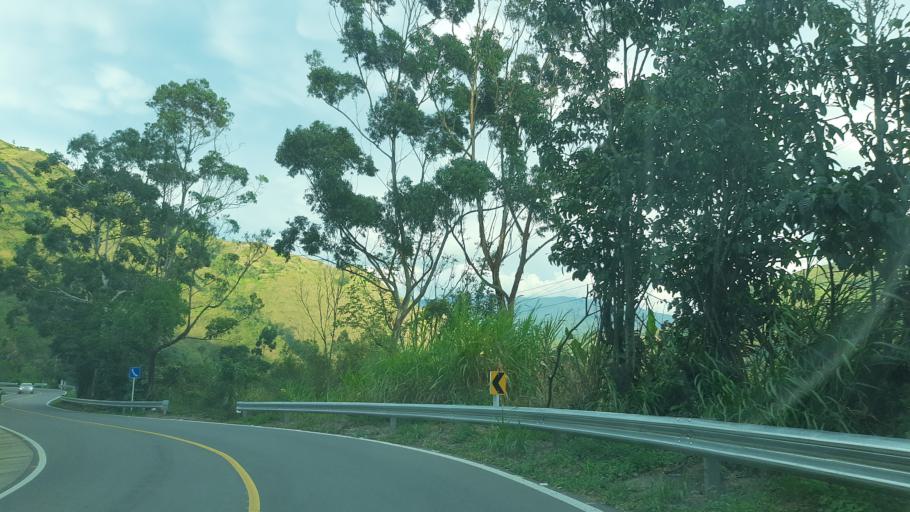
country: CO
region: Boyaca
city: Somondoco
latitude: 5.0075
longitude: -73.4372
